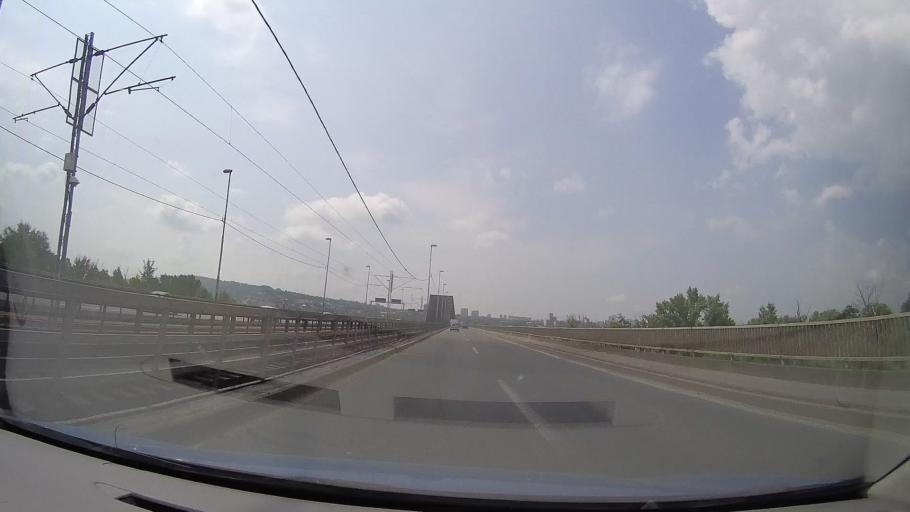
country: RS
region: Central Serbia
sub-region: Belgrade
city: Palilula
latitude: 44.8344
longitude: 20.4929
